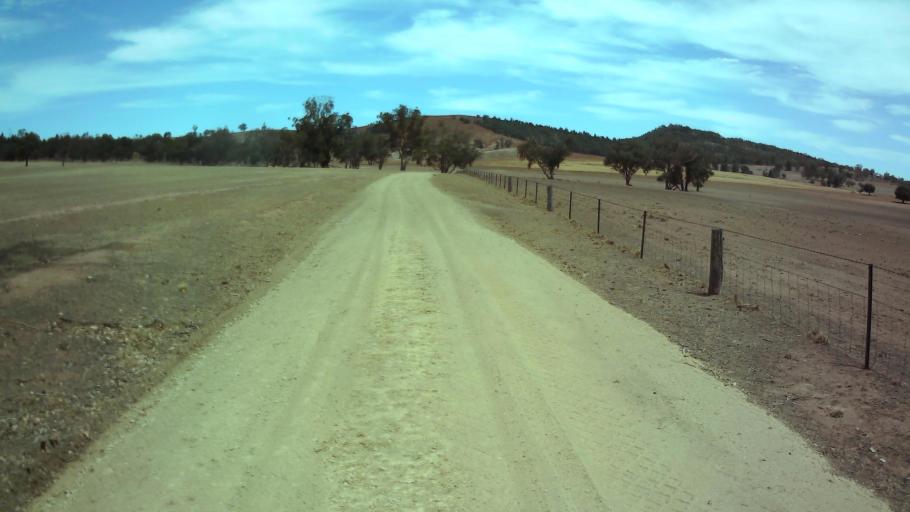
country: AU
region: New South Wales
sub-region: Weddin
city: Grenfell
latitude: -33.7817
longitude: 148.1514
